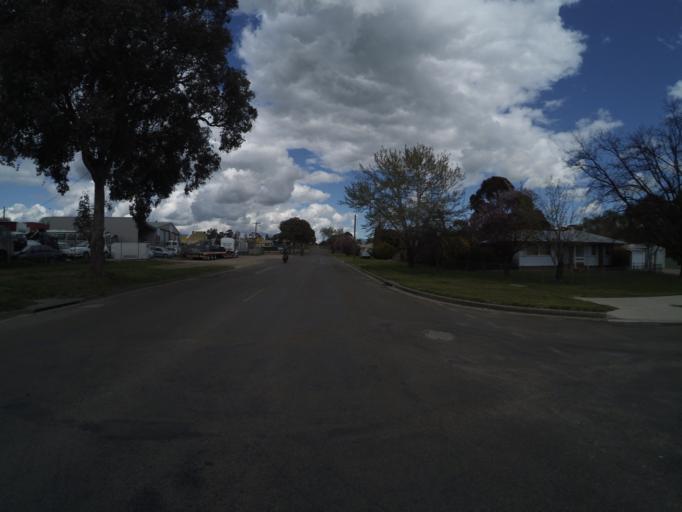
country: AU
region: New South Wales
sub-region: Yass Valley
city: Yass
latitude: -34.8513
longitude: 148.9179
